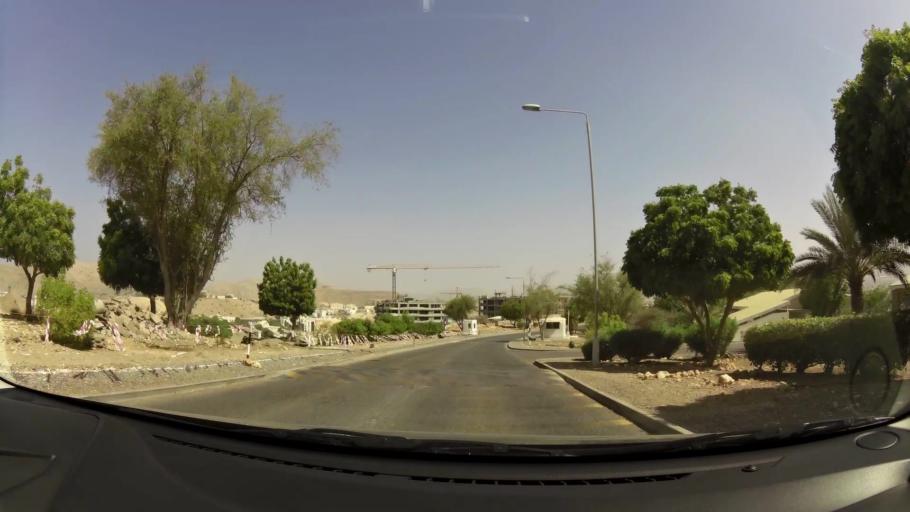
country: OM
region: Muhafazat Masqat
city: Muscat
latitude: 23.6263
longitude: 58.5020
